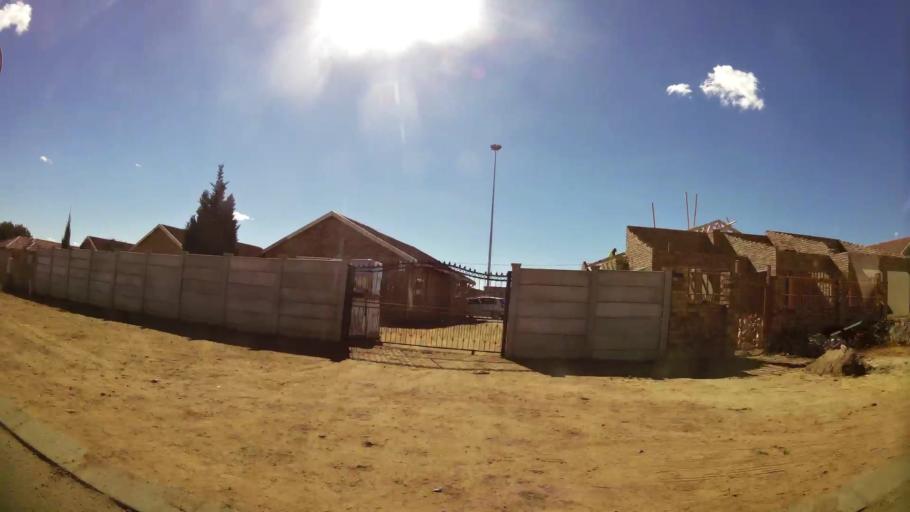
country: ZA
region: North-West
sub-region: Dr Kenneth Kaunda District Municipality
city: Klerksdorp
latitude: -26.8765
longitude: 26.5807
